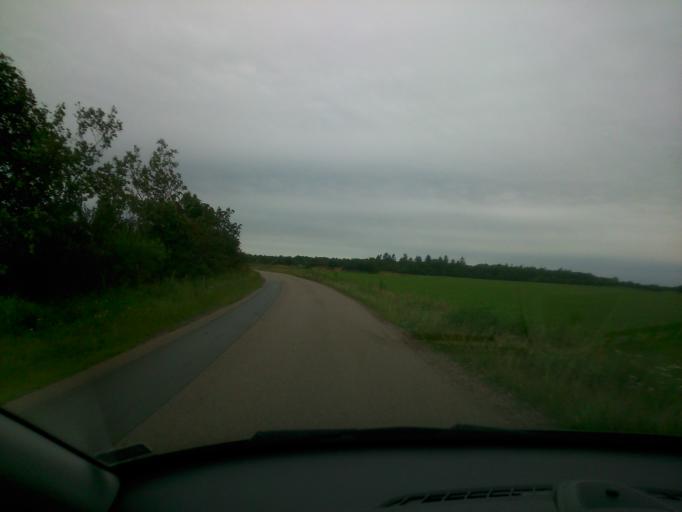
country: DK
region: Central Jutland
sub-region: Ringkobing-Skjern Kommune
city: Skjern
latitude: 55.9884
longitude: 8.3848
